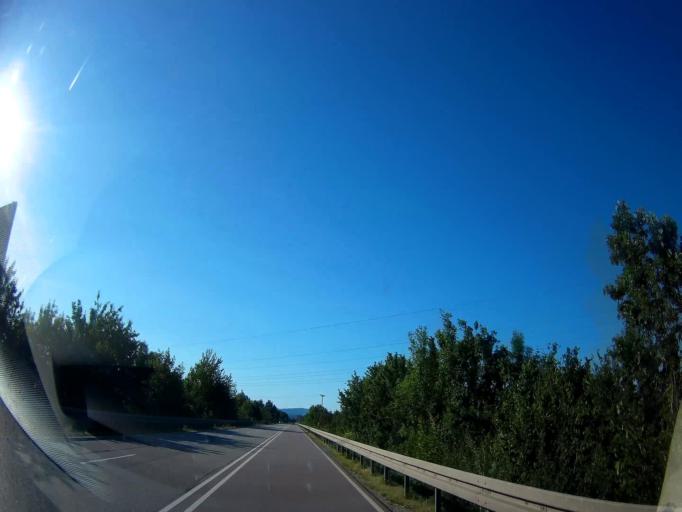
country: DE
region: Bavaria
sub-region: Lower Bavaria
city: Alterhofen
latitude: 48.8763
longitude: 12.6234
